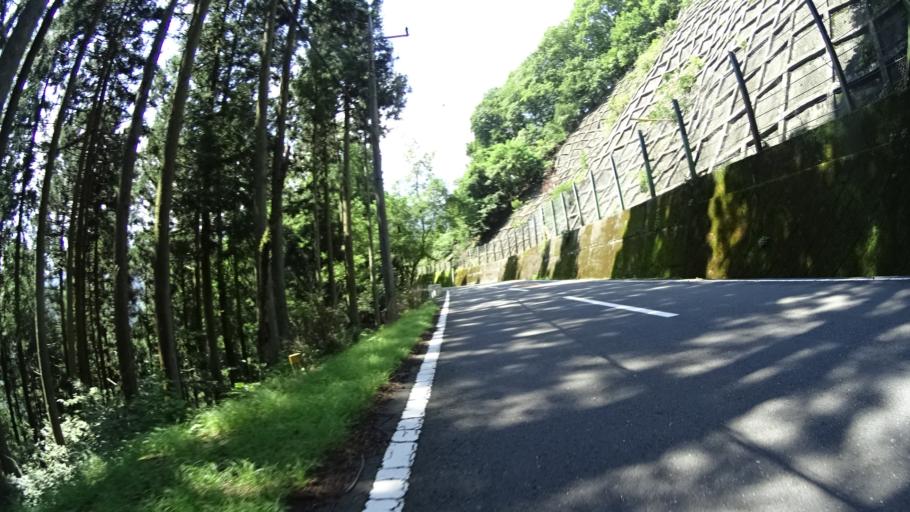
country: JP
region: Gunma
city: Tomioka
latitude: 36.0618
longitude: 138.8511
